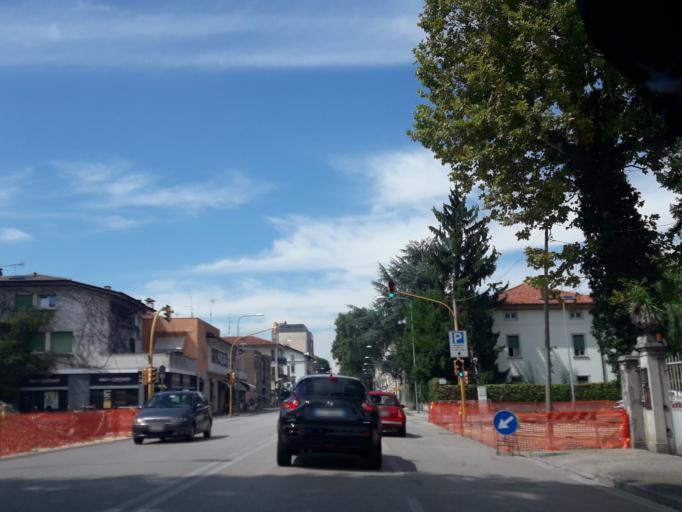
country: IT
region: Friuli Venezia Giulia
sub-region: Provincia di Udine
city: Udine
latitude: 46.0521
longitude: 13.2475
